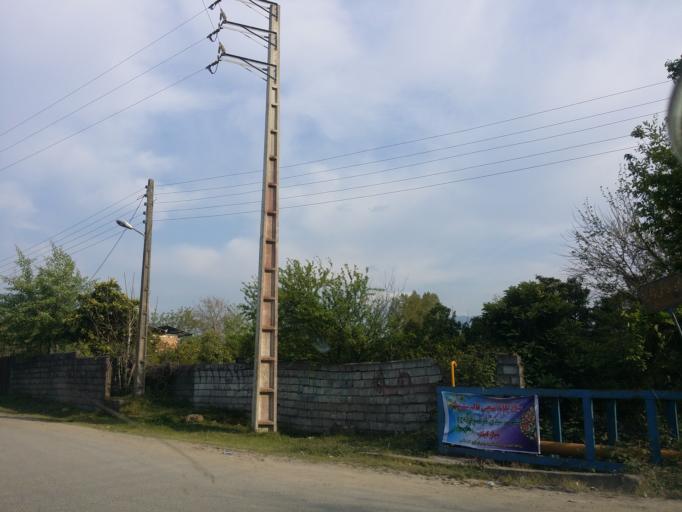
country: IR
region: Mazandaran
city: Chalus
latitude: 36.6576
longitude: 51.3906
